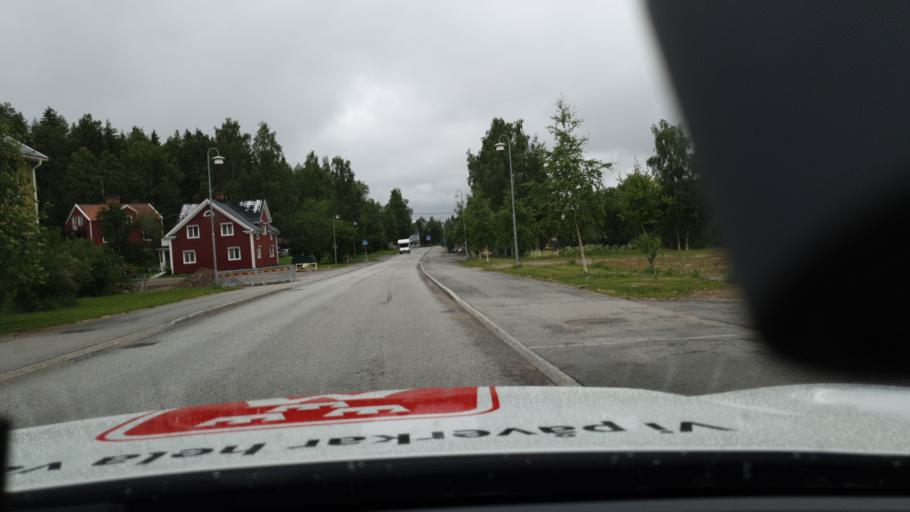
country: SE
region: Norrbotten
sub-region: Overtornea Kommun
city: OEvertornea
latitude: 66.3918
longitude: 23.6565
